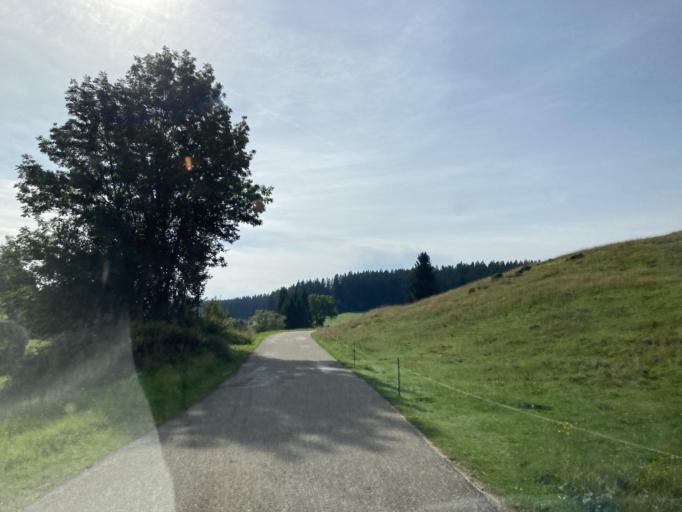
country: DE
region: Baden-Wuerttemberg
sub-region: Freiburg Region
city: Schonwald im Schwarzwald
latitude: 48.0999
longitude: 8.2138
